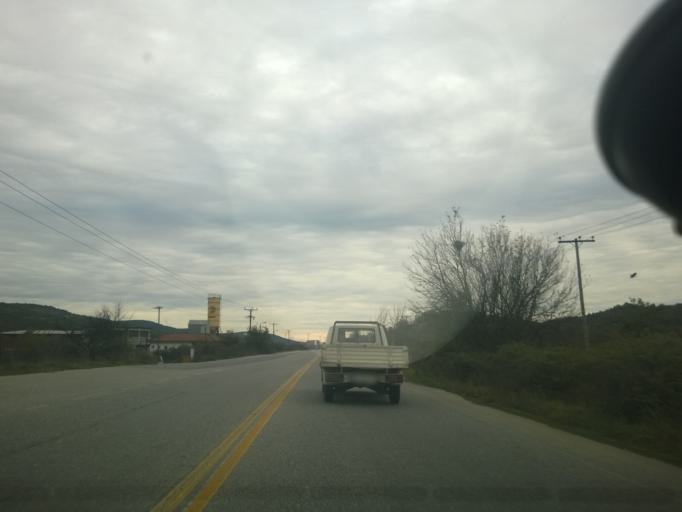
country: GR
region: Central Macedonia
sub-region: Nomos Pellis
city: Apsalos
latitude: 40.8825
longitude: 22.0807
